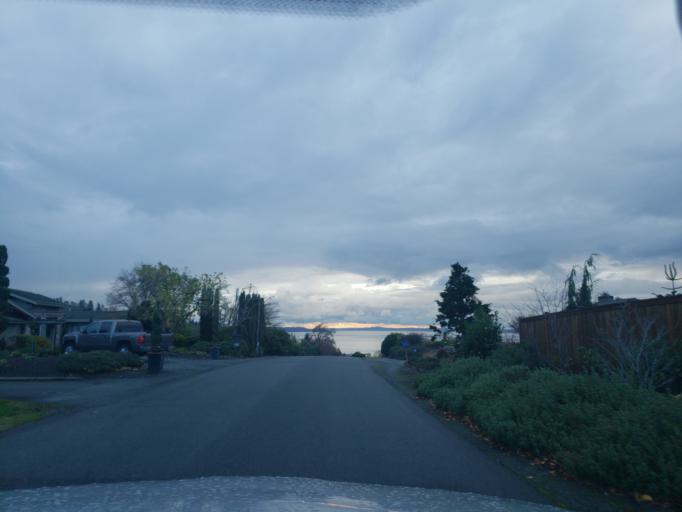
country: US
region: Washington
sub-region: Snohomish County
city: Woodway
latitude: 47.7640
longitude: -122.3776
